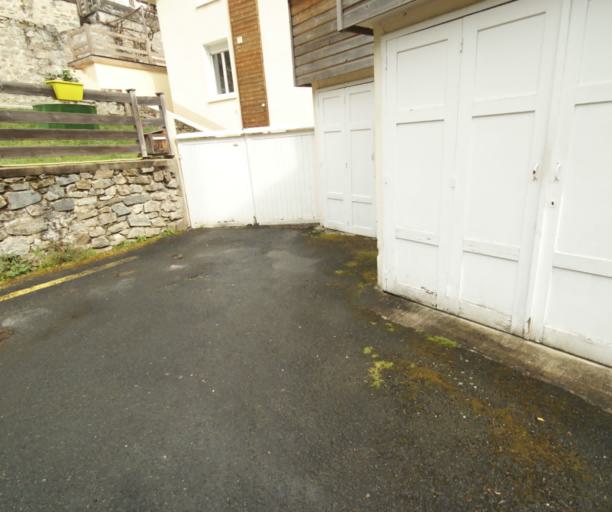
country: FR
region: Limousin
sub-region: Departement de la Correze
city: Tulle
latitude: 45.2644
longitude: 1.7585
